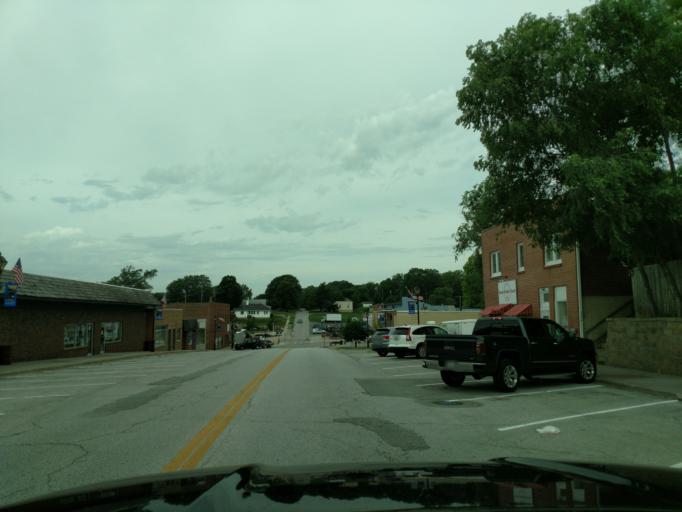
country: US
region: Nebraska
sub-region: Douglas County
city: Ralston
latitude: 41.2016
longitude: -96.0303
